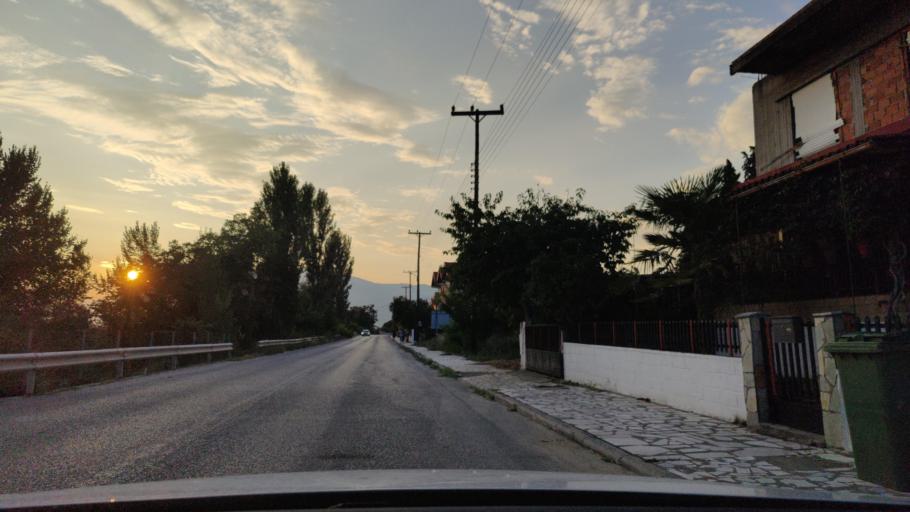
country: GR
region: Central Macedonia
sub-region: Nomos Serron
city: Sidirokastro
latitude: 41.2409
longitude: 23.3869
